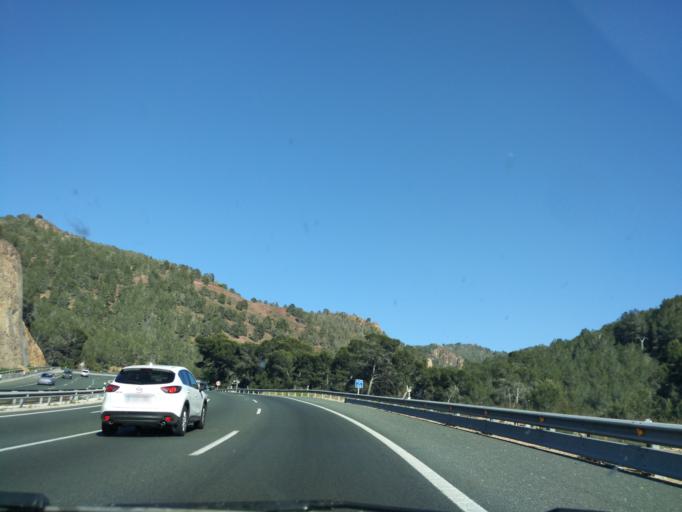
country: ES
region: Murcia
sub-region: Murcia
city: Murcia
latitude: 37.9070
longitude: -1.1551
